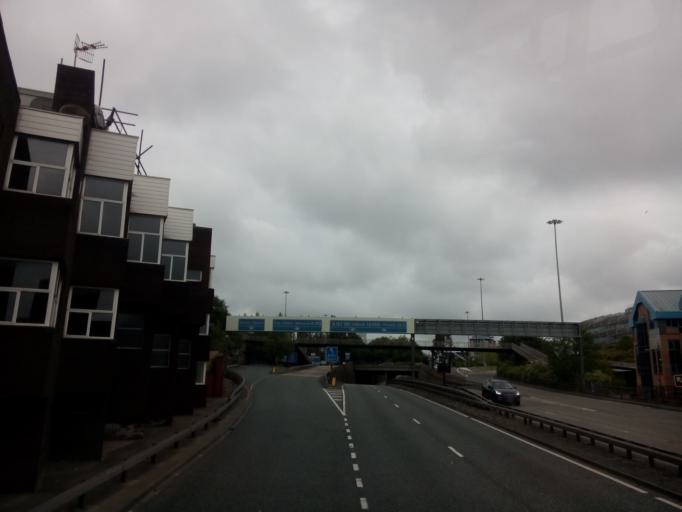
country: GB
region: England
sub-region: Newcastle upon Tyne
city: Newcastle upon Tyne
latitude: 54.9735
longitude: -1.6081
